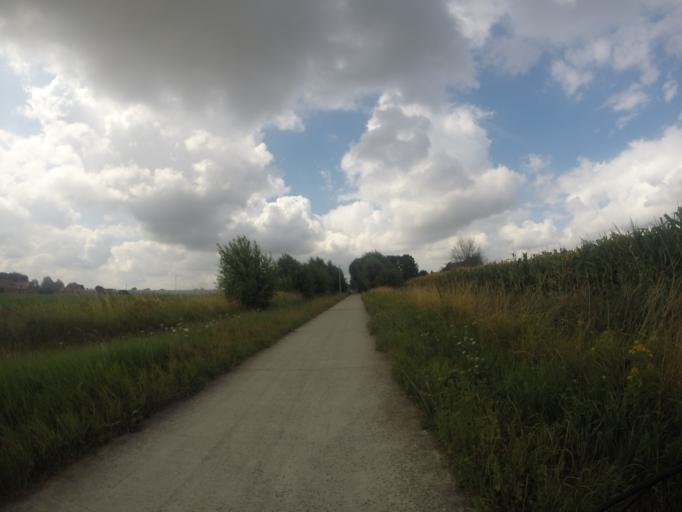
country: BE
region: Flanders
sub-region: Provincie West-Vlaanderen
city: Moorslede
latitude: 50.9177
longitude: 3.0835
